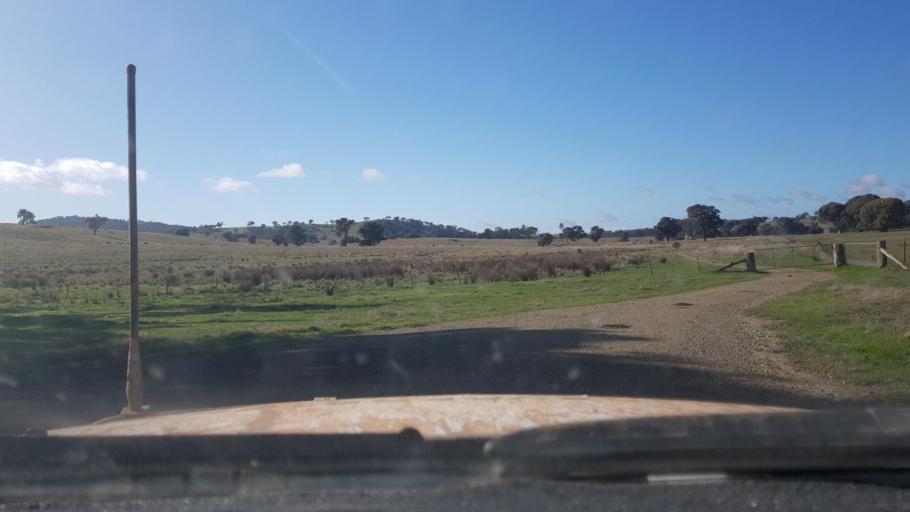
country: AU
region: New South Wales
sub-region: Gundagai
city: Gundagai
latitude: -34.8985
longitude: 147.9554
